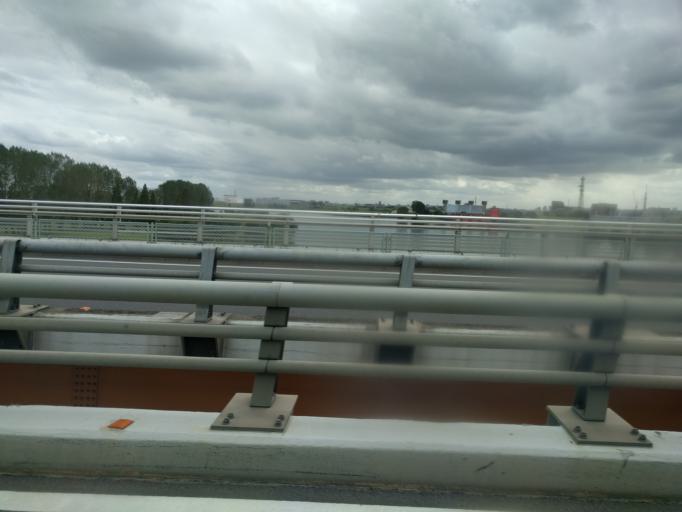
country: JP
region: Saitama
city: Kawaguchi
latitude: 35.7901
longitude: 139.7242
